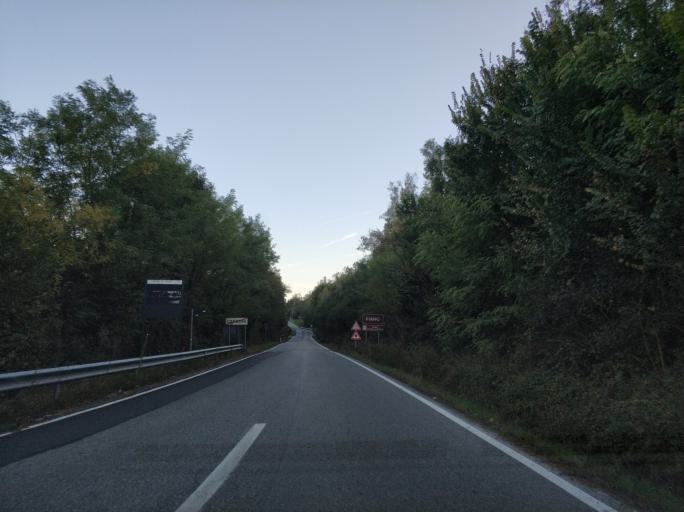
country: IT
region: Piedmont
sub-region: Provincia di Torino
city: Cafasse
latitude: 45.2350
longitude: 7.5243
